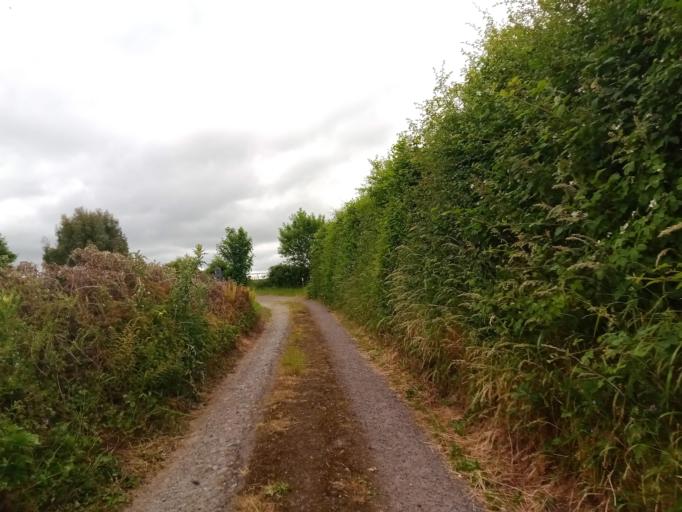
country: IE
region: Leinster
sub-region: Laois
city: Rathdowney
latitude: 52.7759
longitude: -7.4675
